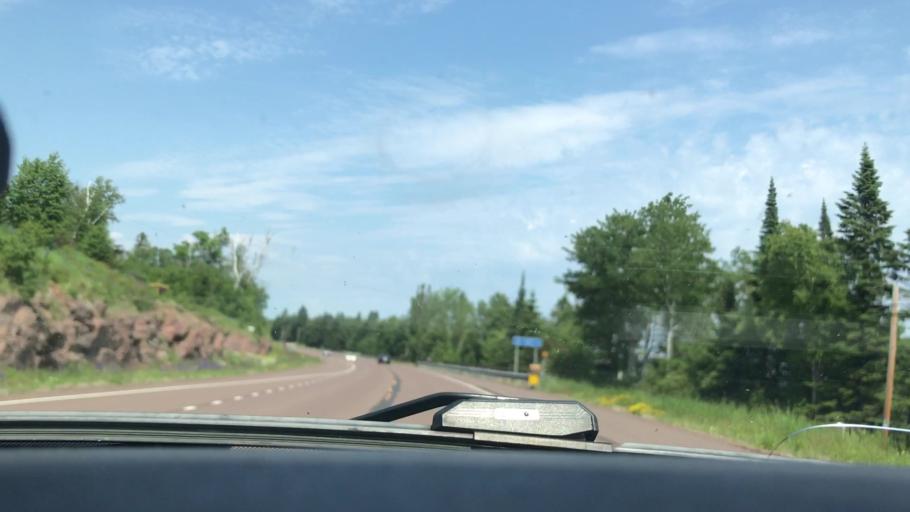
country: US
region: Minnesota
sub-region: Cook County
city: Grand Marais
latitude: 47.6093
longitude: -90.7680
